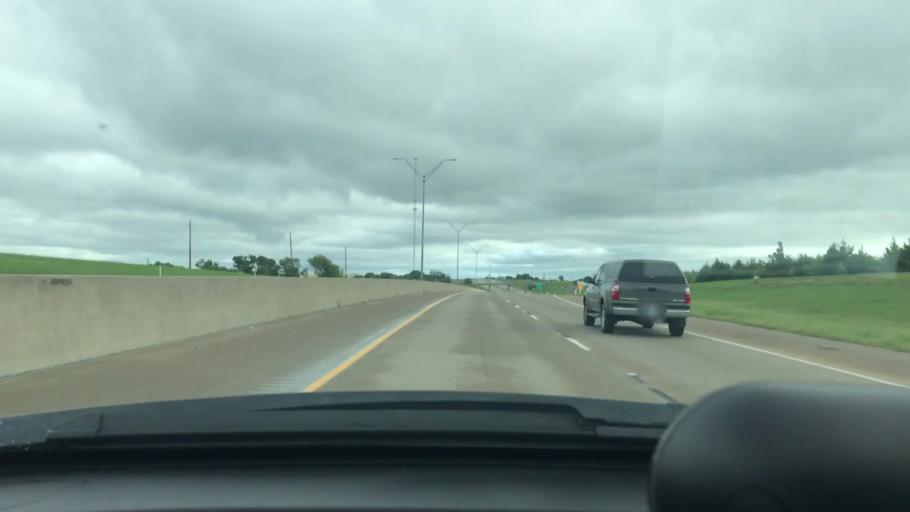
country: US
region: Texas
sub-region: Grayson County
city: Howe
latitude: 33.5224
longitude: -96.6145
